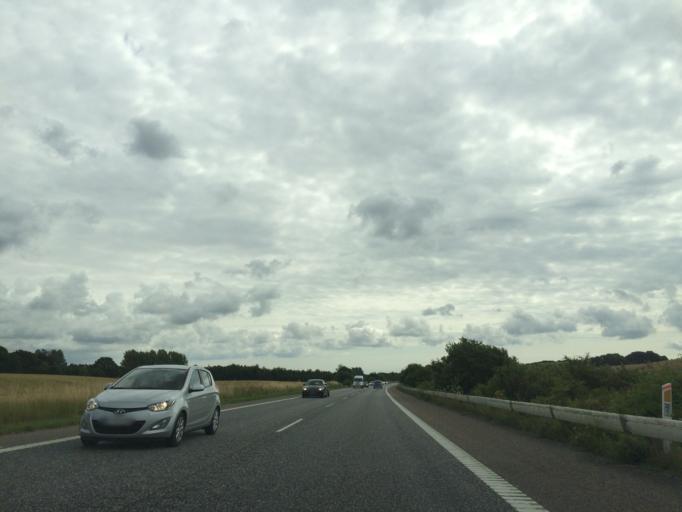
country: DK
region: Central Jutland
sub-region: Syddjurs Kommune
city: Ronde
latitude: 56.3177
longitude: 10.4737
